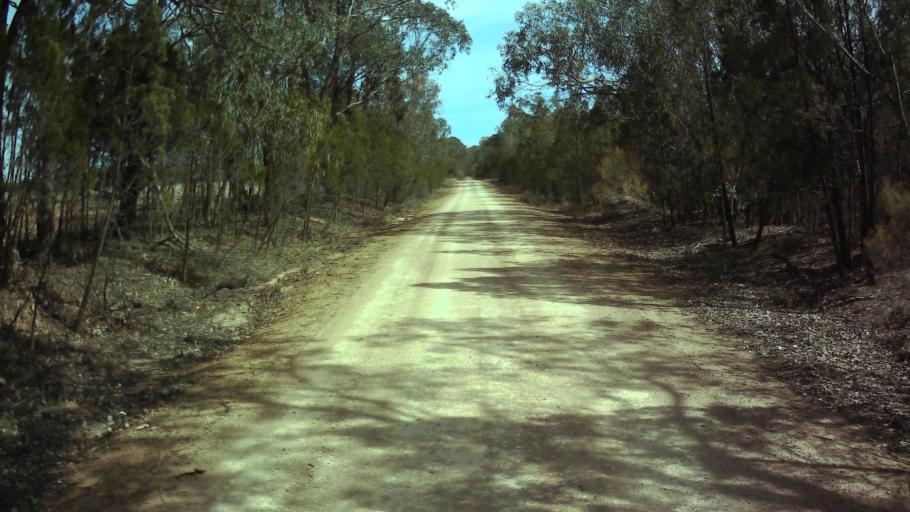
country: AU
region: New South Wales
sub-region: Weddin
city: Grenfell
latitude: -33.8745
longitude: 148.1485
